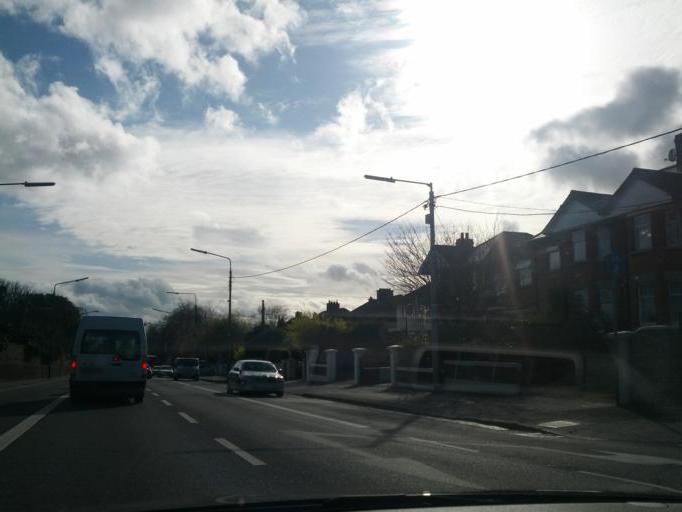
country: IE
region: Leinster
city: Beaumont
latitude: 53.3808
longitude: -6.2455
